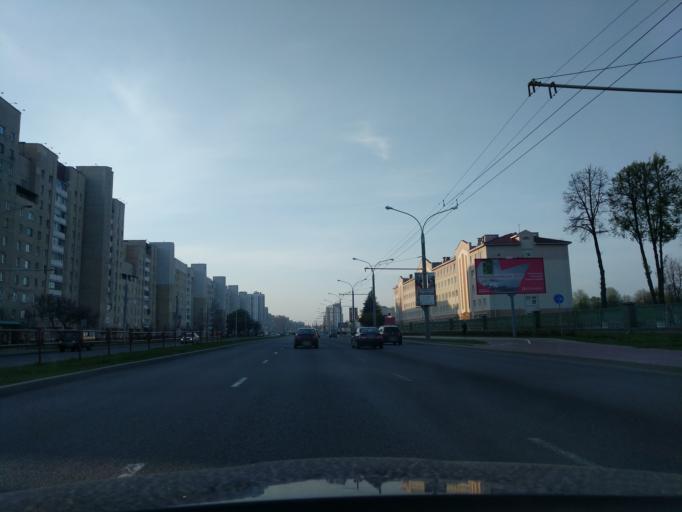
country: BY
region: Minsk
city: Minsk
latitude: 53.8663
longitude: 27.5708
